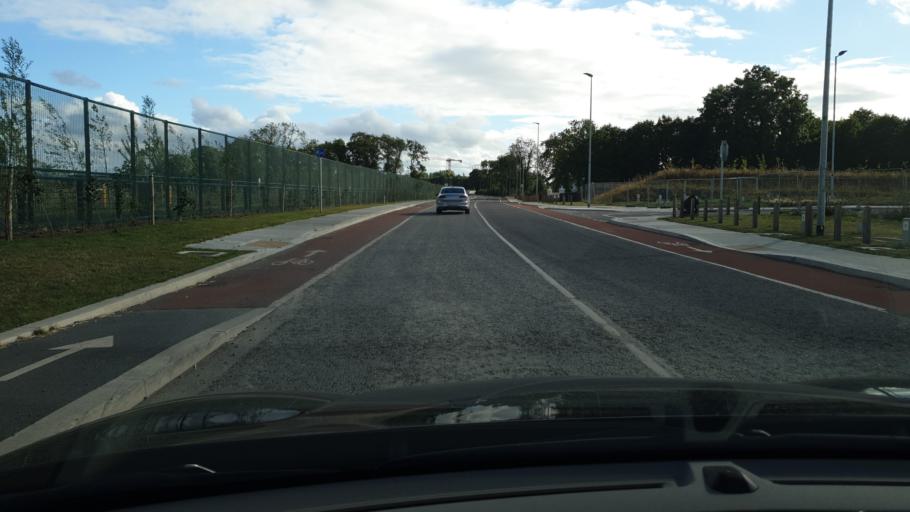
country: IE
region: Leinster
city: Hartstown
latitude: 53.4186
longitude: -6.4386
